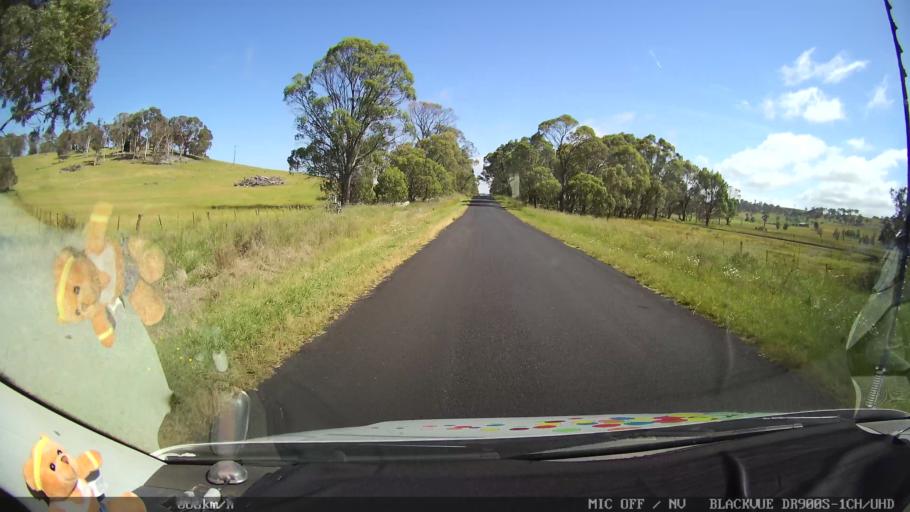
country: AU
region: New South Wales
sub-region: Guyra
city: Guyra
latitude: -30.0896
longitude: 151.6783
